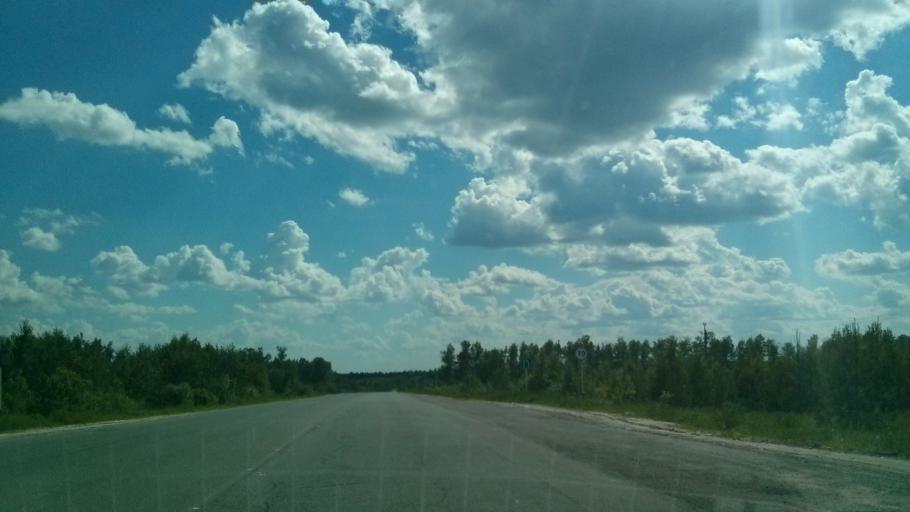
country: RU
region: Vladimir
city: Melenki
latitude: 55.3374
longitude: 41.6651
